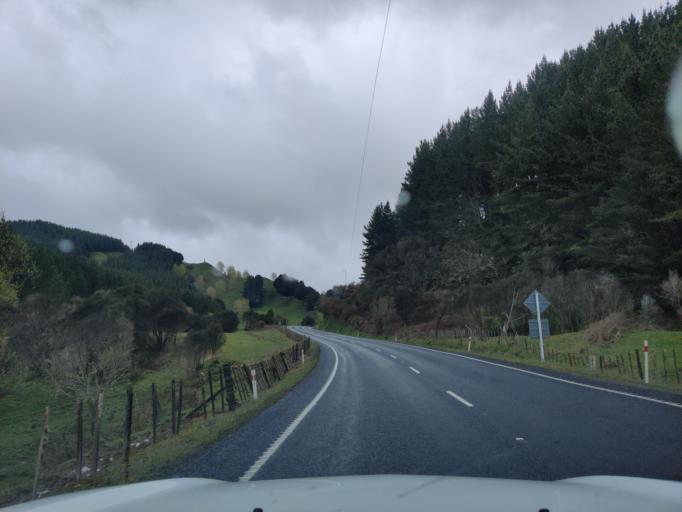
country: NZ
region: Waikato
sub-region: Otorohanga District
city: Otorohanga
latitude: -38.6622
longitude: 175.2066
